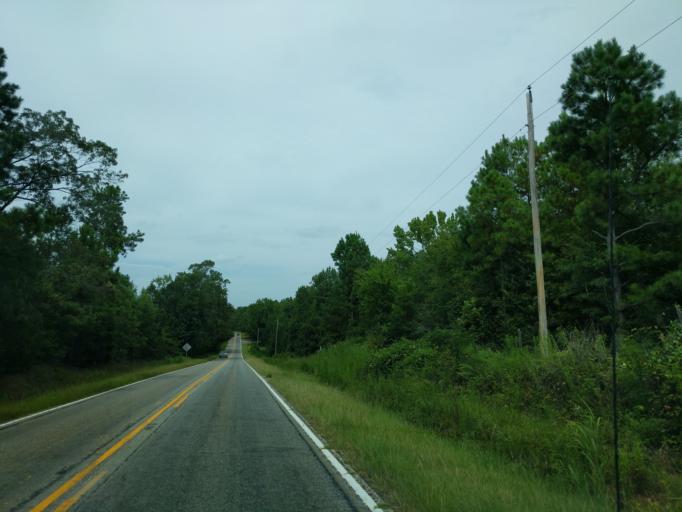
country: US
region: South Carolina
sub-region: Abbeville County
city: Calhoun Falls
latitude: 34.1255
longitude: -82.5945
